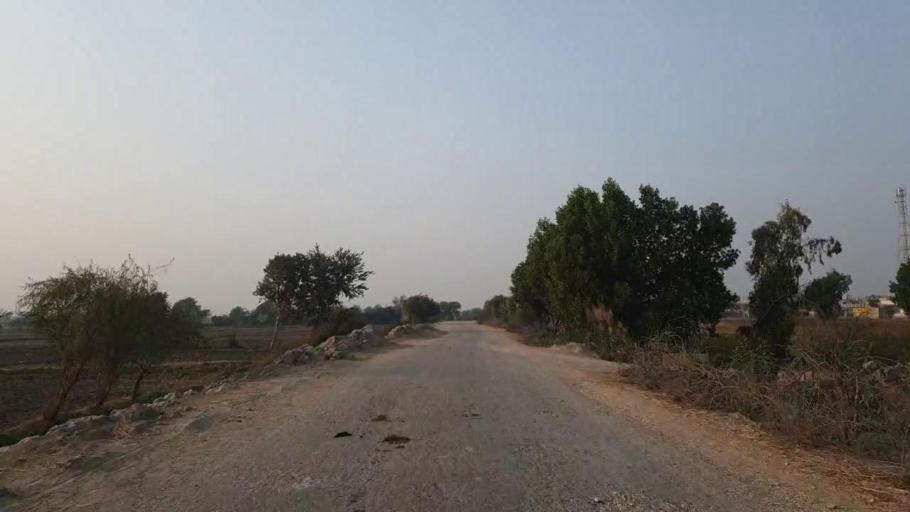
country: PK
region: Sindh
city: Tando Muhammad Khan
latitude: 25.0917
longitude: 68.4345
